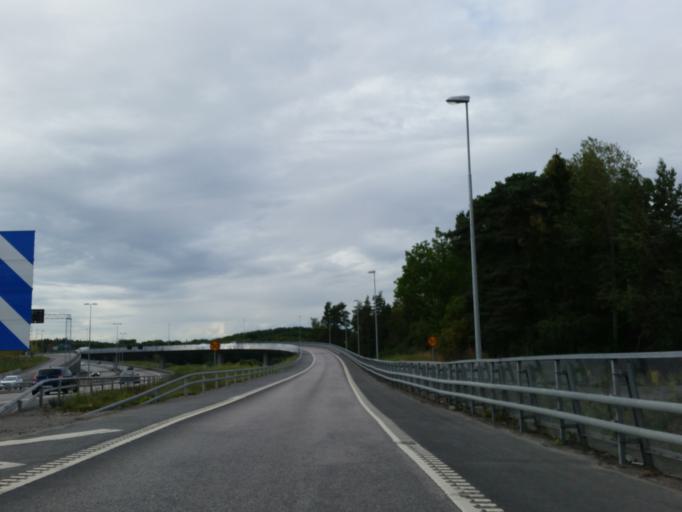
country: SE
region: Stockholm
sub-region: Stockholms Kommun
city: Kista
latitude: 59.3966
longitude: 17.9144
